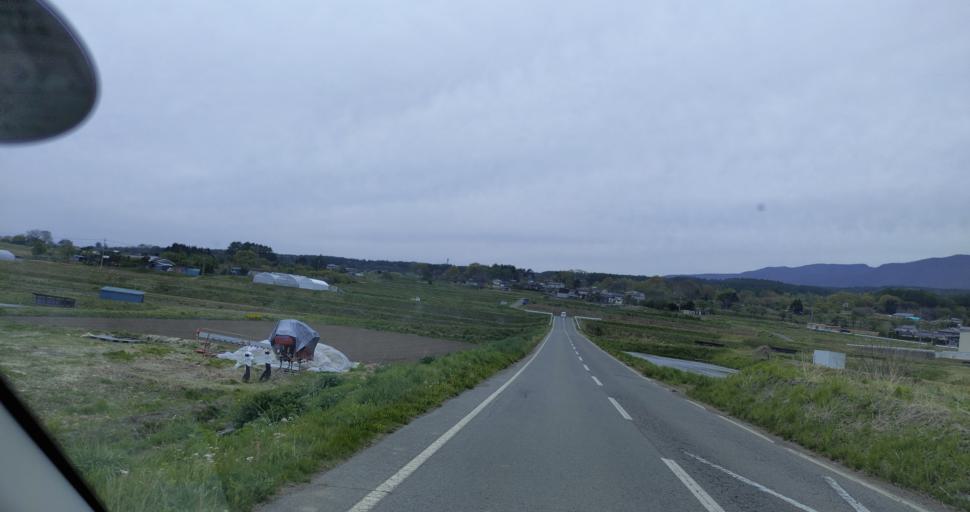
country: JP
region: Nagano
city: Komoro
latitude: 36.3329
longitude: 138.4889
